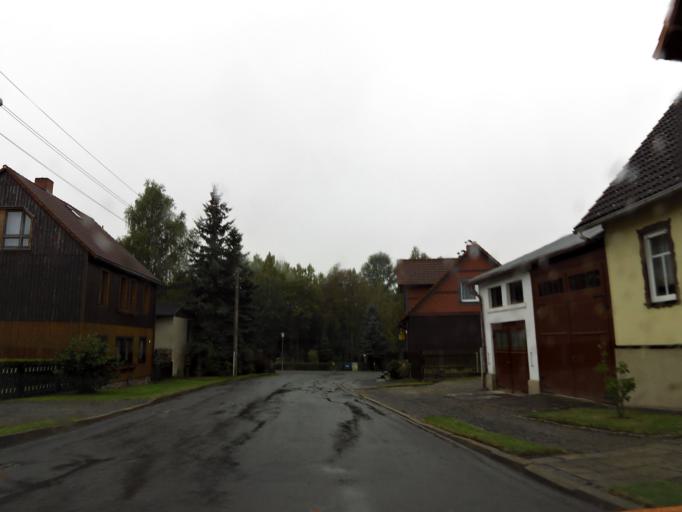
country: DE
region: Saxony-Anhalt
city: Hasselfelde
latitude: 51.6624
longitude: 10.8827
